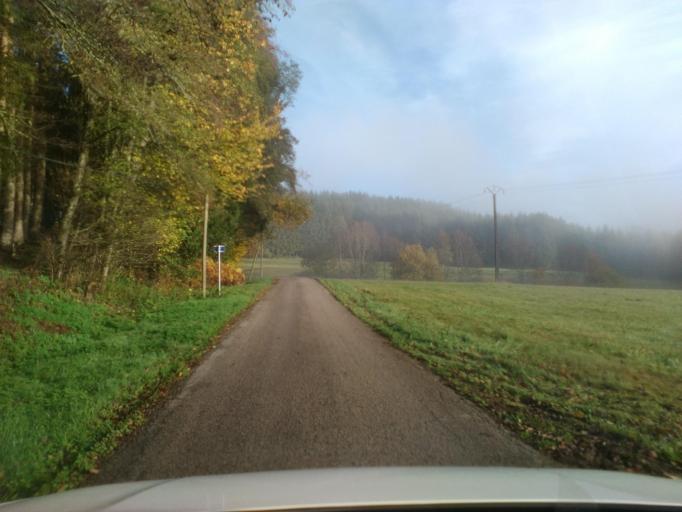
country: FR
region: Lorraine
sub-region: Departement des Vosges
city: Senones
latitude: 48.4170
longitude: 7.0007
